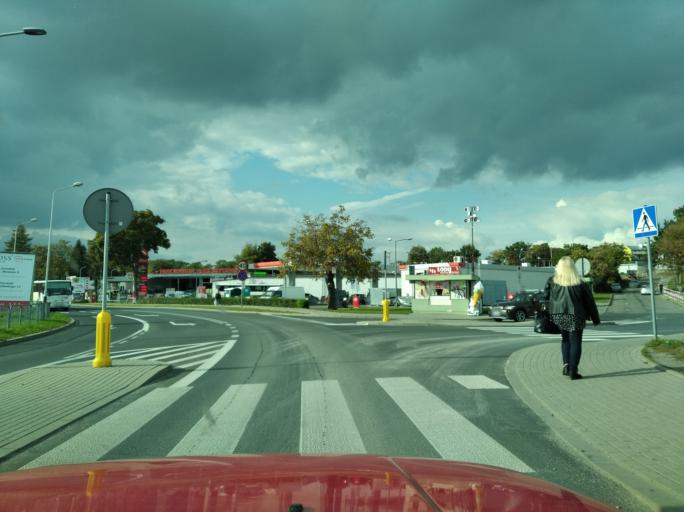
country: PL
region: Subcarpathian Voivodeship
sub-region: Powiat jaroslawski
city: Jaroslaw
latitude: 50.0088
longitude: 22.6765
